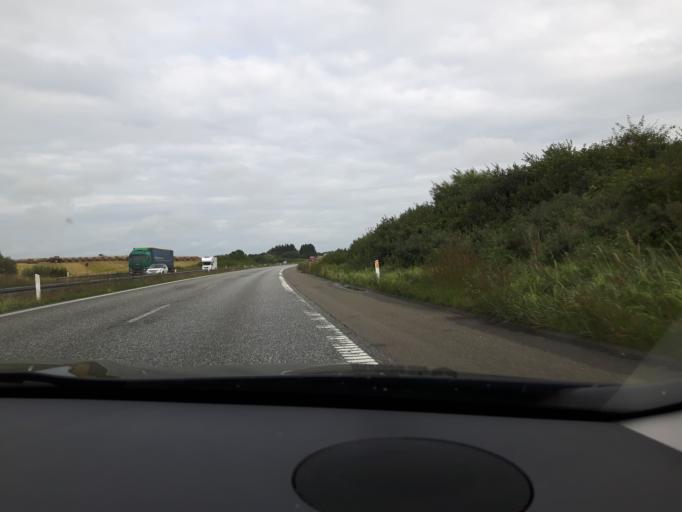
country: DK
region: North Denmark
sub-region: Hjorring Kommune
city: Hirtshals
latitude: 57.5449
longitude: 10.0062
